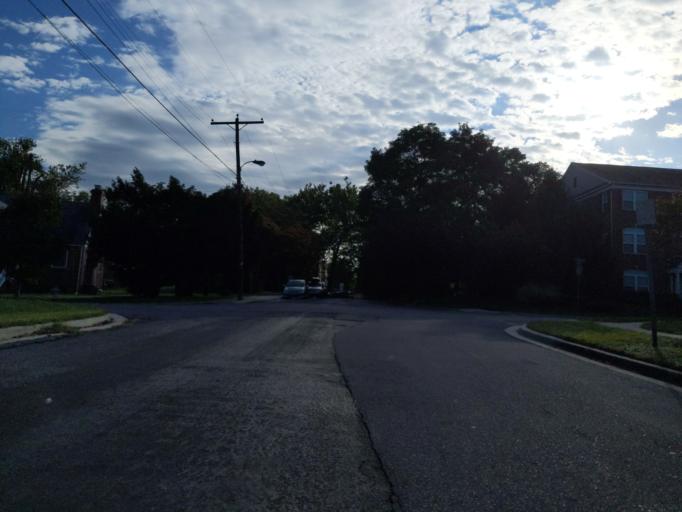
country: US
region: Maryland
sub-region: Montgomery County
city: Forest Glen
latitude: 39.0187
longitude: -77.0476
